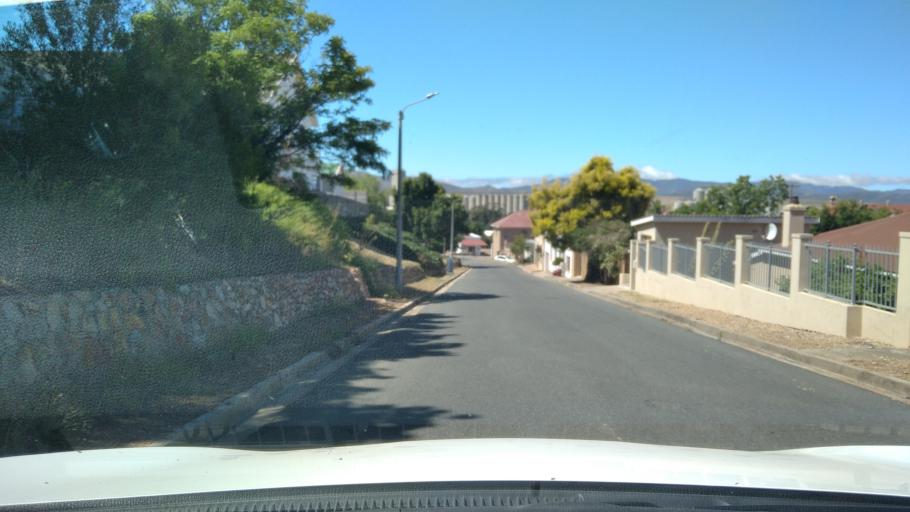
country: ZA
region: Western Cape
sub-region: Overberg District Municipality
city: Caledon
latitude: -34.2299
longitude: 19.4304
